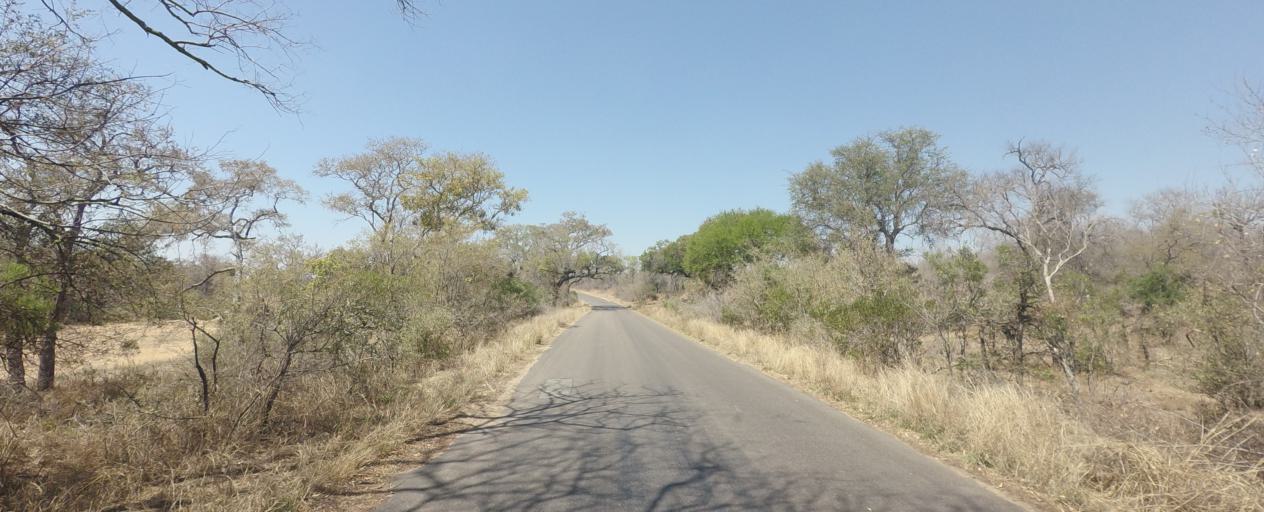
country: ZA
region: Limpopo
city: Thulamahashi
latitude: -24.4153
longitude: 31.5193
